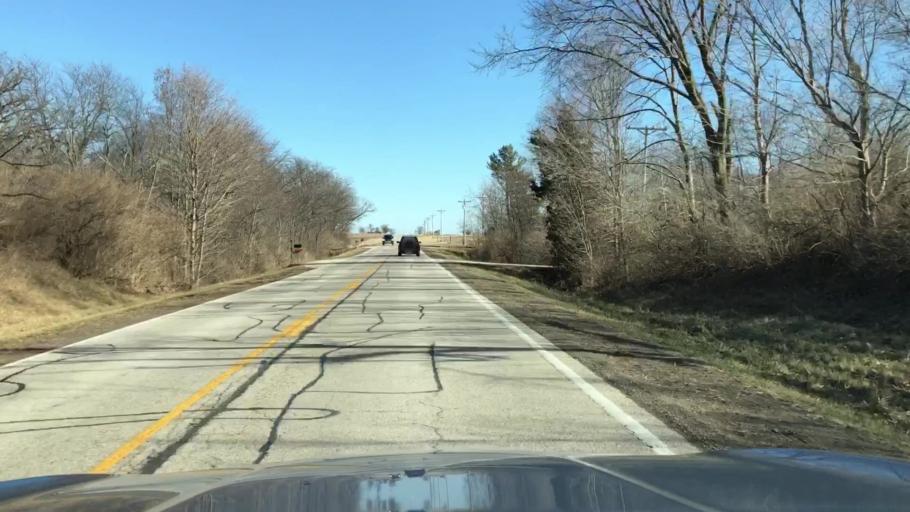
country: US
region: Illinois
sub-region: McLean County
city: Lexington
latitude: 40.6451
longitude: -88.8333
